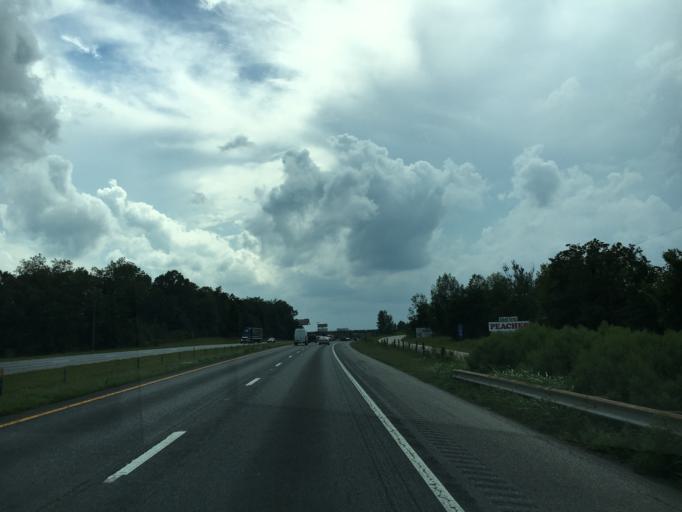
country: US
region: South Carolina
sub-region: Spartanburg County
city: Cowpens
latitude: 35.0578
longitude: -81.7842
